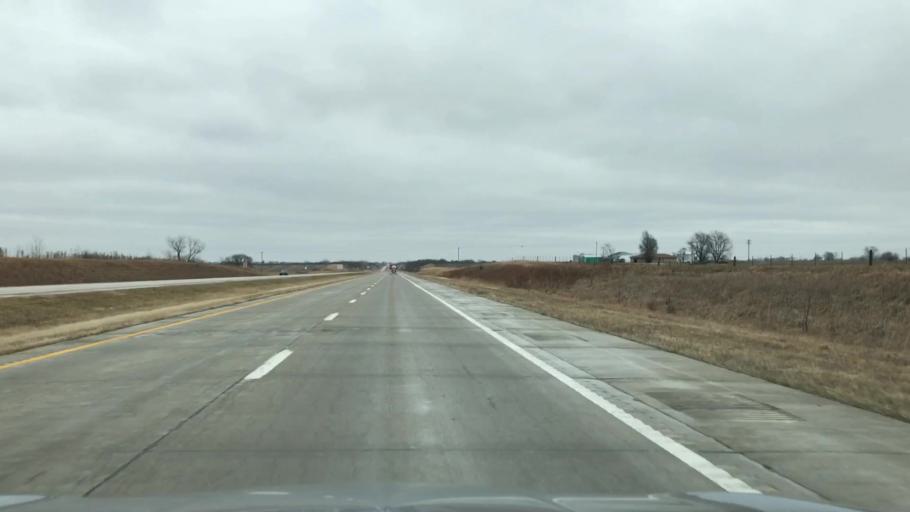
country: US
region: Missouri
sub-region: Caldwell County
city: Hamilton
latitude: 39.7336
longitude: -93.9886
